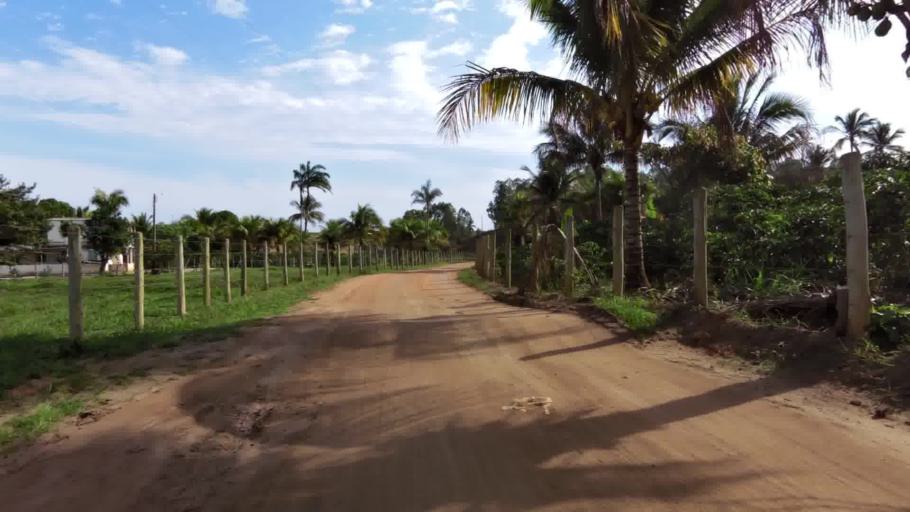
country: BR
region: Espirito Santo
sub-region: Piuma
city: Piuma
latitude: -20.8197
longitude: -40.7410
